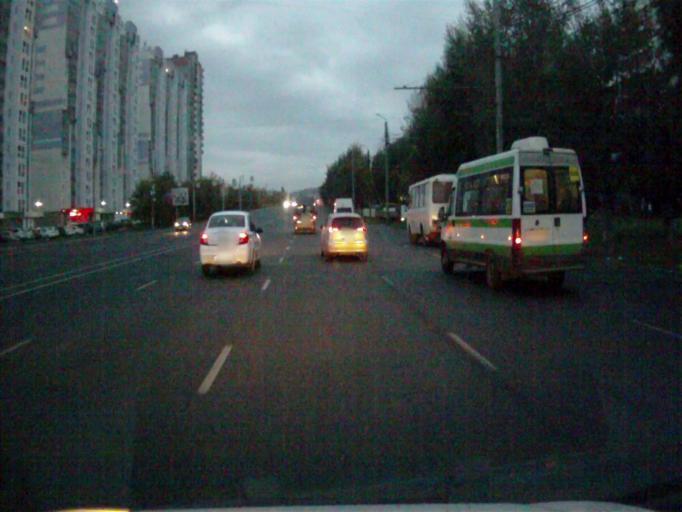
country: RU
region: Chelyabinsk
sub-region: Gorod Chelyabinsk
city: Chelyabinsk
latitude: 55.1786
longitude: 61.3309
